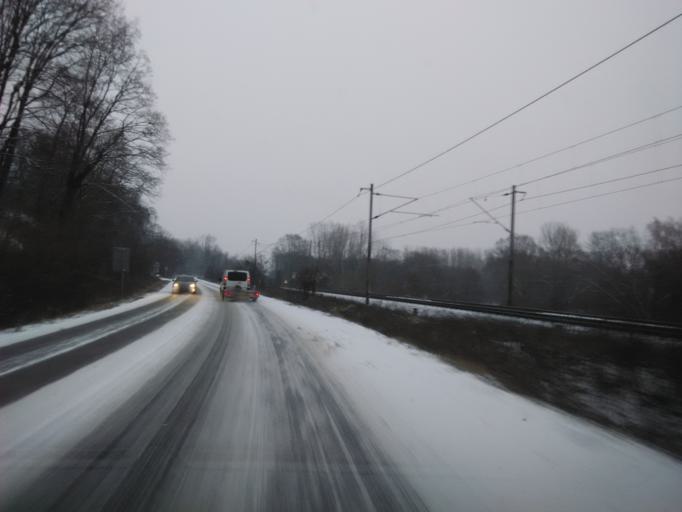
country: CZ
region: Olomoucky
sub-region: Okres Prerov
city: Hranice
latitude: 49.5270
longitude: 17.7546
